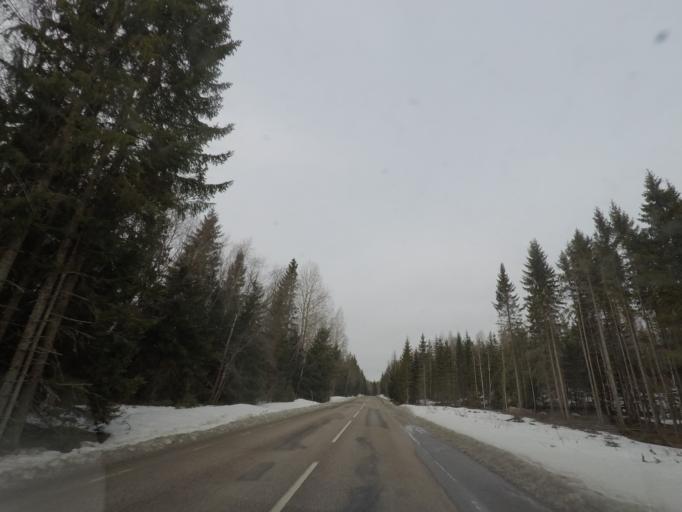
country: SE
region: Vaestmanland
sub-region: Vasteras
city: Skultuna
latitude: 59.7426
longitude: 16.3729
